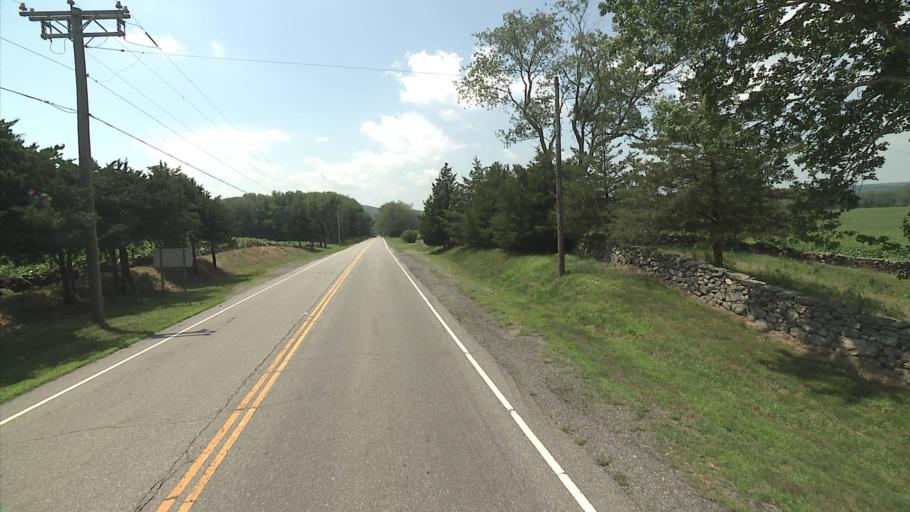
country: US
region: Connecticut
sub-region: New London County
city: Preston City
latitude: 41.5524
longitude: -71.8862
